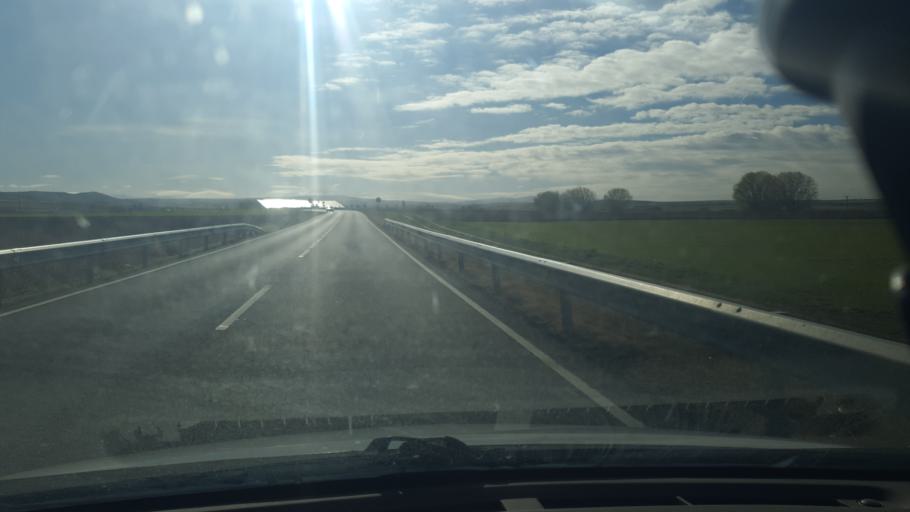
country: ES
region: Castille and Leon
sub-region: Provincia de Avila
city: Gotarrendura
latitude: 40.8119
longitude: -4.7553
